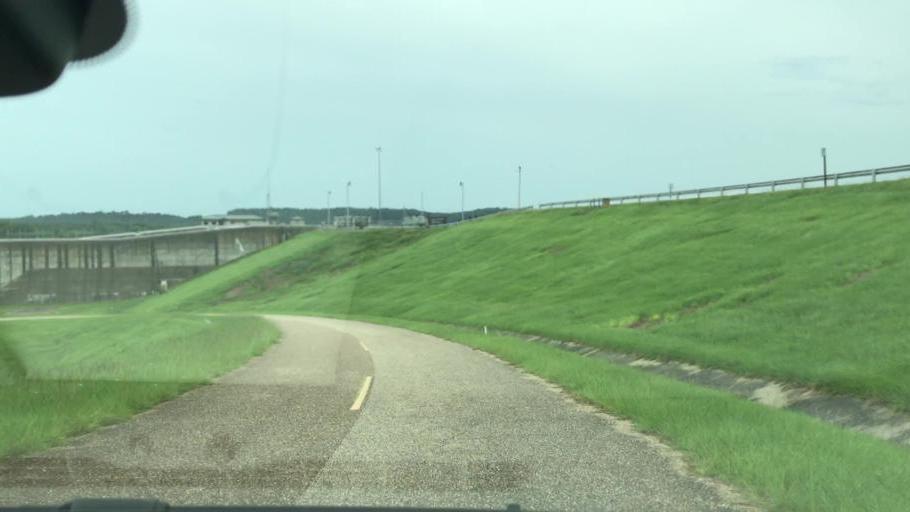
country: US
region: Georgia
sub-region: Clay County
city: Fort Gaines
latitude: 31.6284
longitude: -85.0607
